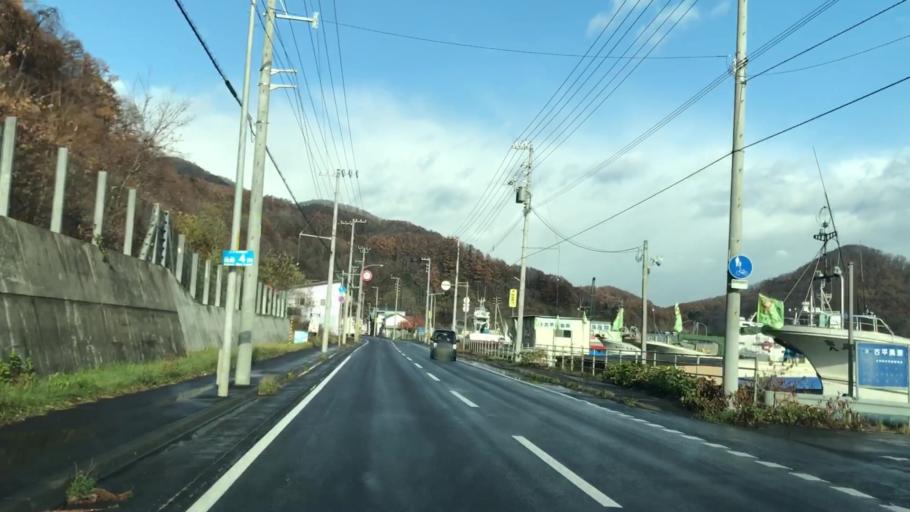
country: JP
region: Hokkaido
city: Yoichi
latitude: 43.2699
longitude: 140.6375
